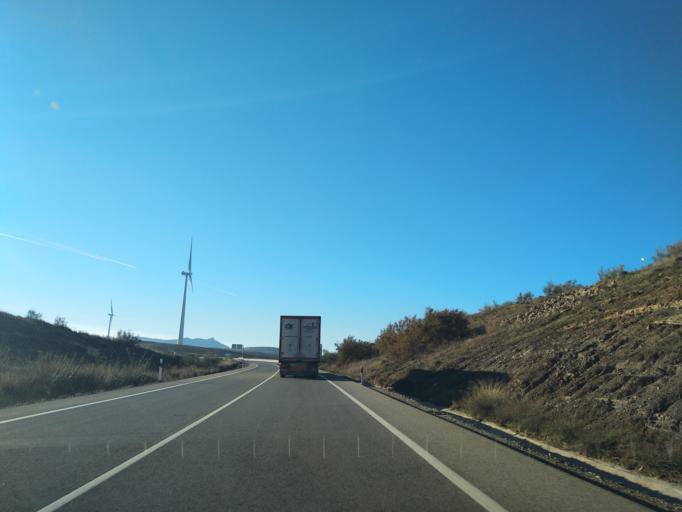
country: ES
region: Andalusia
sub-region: Provincia de Malaga
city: Teba
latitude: 36.9442
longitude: -4.8669
